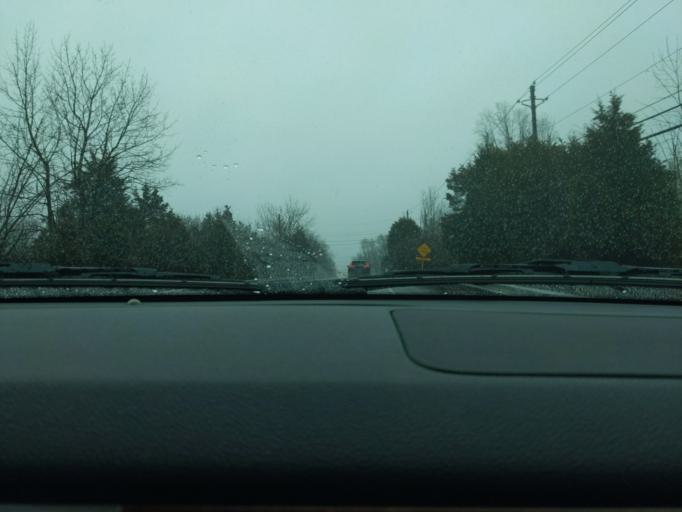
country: US
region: Pennsylvania
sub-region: Bucks County
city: Perkasie
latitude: 40.4092
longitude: -75.2623
